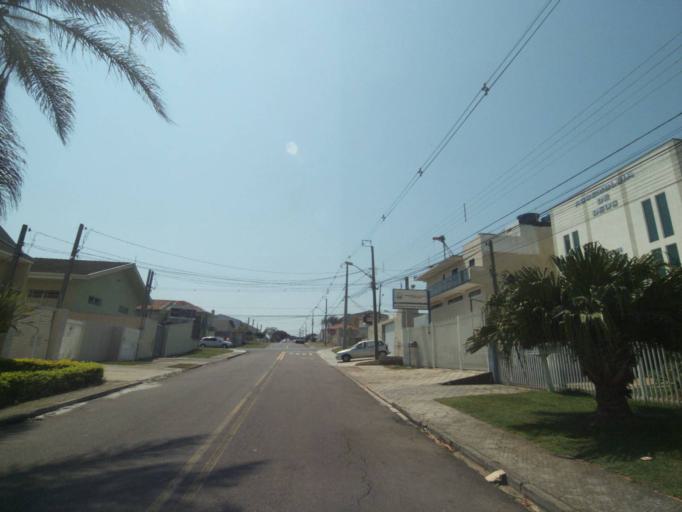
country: BR
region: Parana
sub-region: Sao Jose Dos Pinhais
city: Sao Jose dos Pinhais
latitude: -25.5158
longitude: -49.2678
